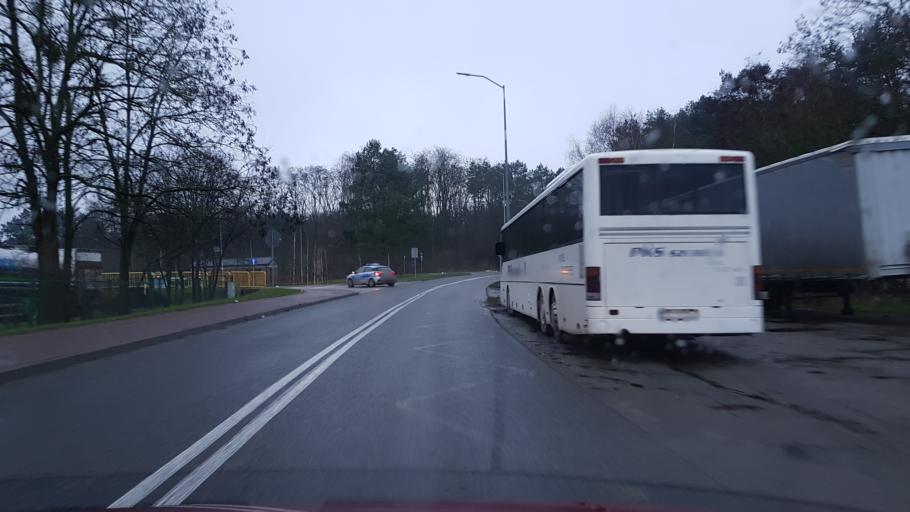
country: PL
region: West Pomeranian Voivodeship
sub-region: Powiat policki
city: Police
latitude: 53.5371
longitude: 14.5468
